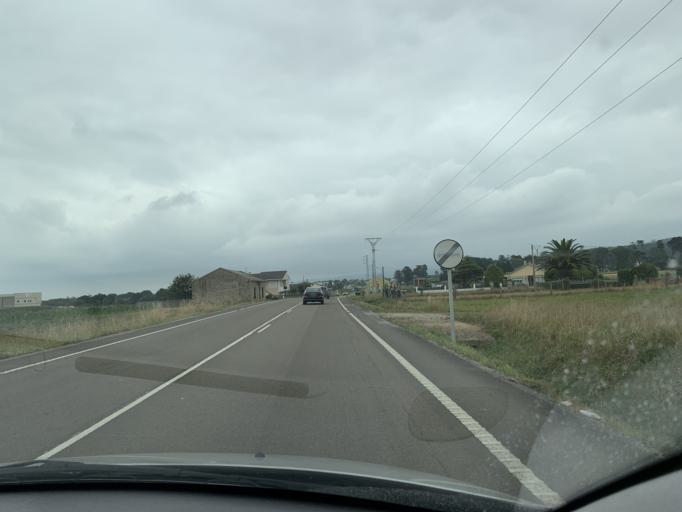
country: ES
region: Galicia
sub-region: Provincia de Lugo
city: Ribadeo
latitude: 43.5457
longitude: -7.0894
